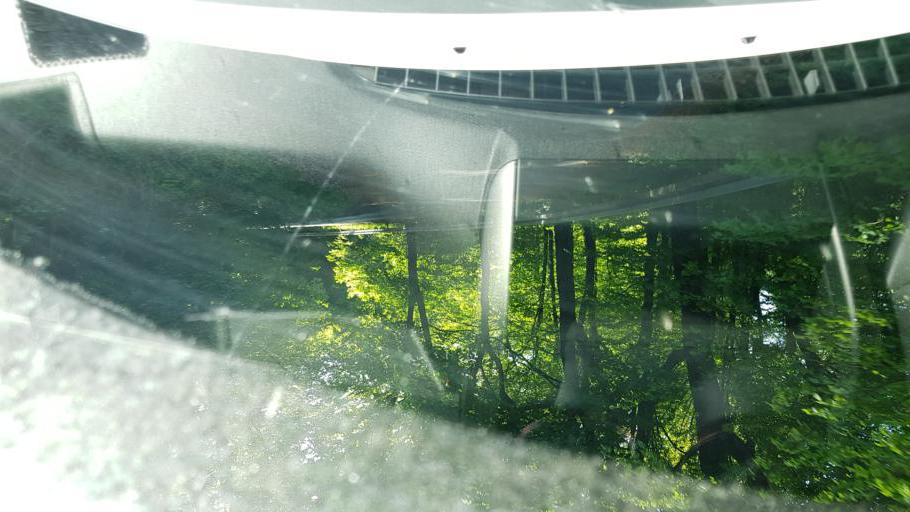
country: PL
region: West Pomeranian Voivodeship
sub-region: Powiat kolobrzeski
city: Goscino
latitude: 54.0118
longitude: 15.6195
